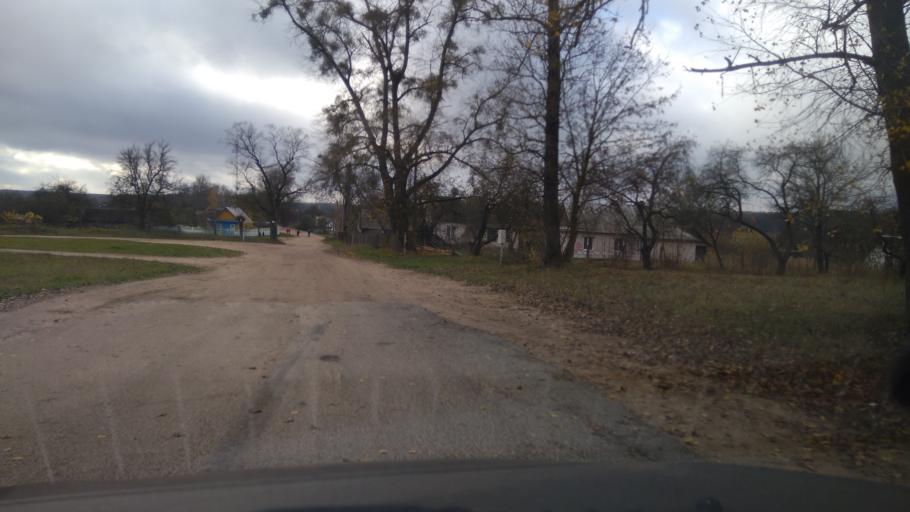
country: BY
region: Minsk
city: Staryya Darohi
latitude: 53.2111
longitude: 28.0484
